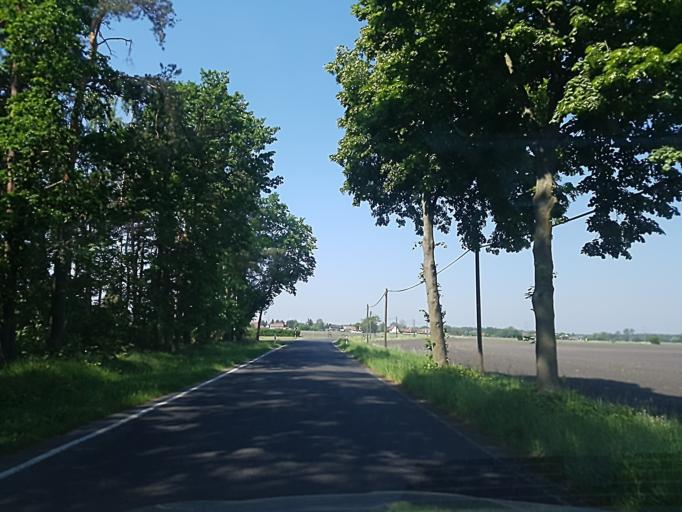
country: DE
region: Brandenburg
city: Schilda
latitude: 51.5880
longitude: 13.3970
